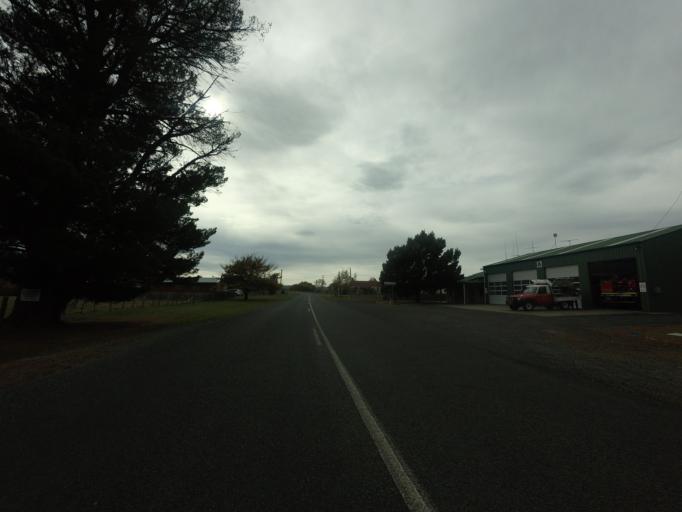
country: AU
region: Tasmania
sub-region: Derwent Valley
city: New Norfolk
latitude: -42.3824
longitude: 147.0030
